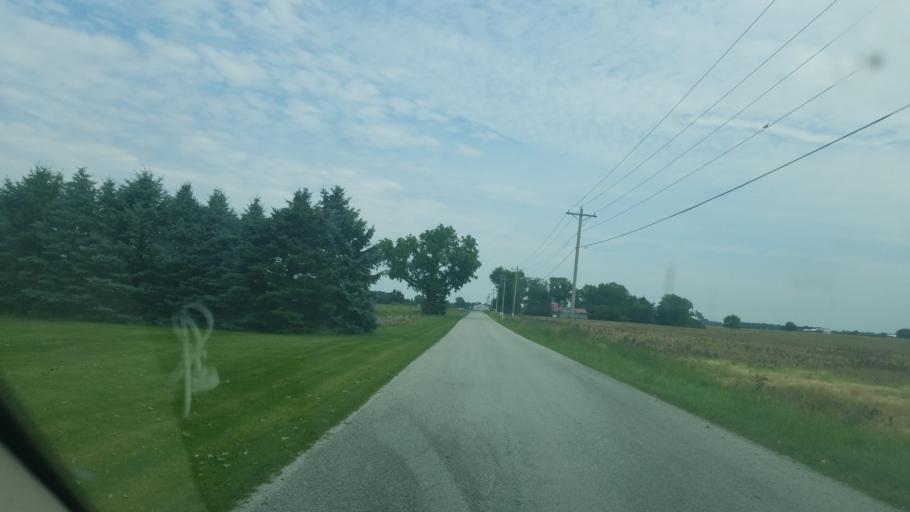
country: US
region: Ohio
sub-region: Seneca County
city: Fostoria
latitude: 41.0504
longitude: -83.4641
